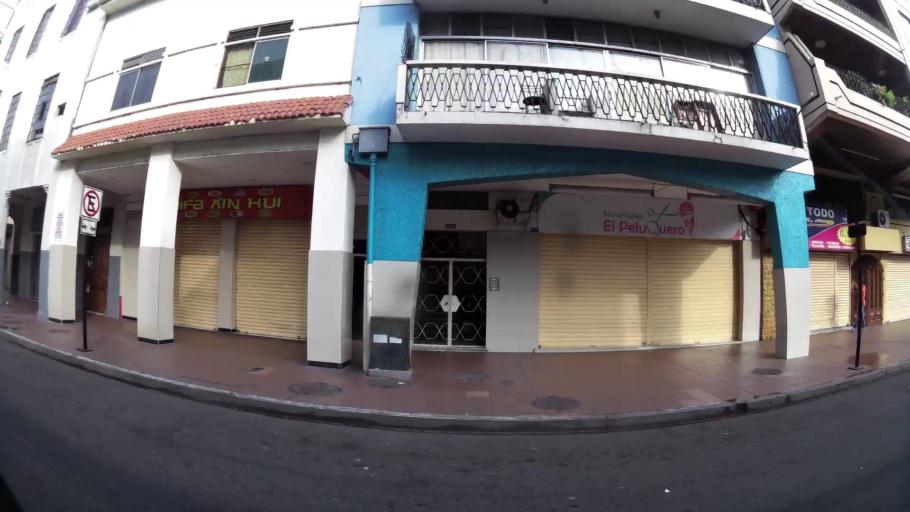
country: EC
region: Guayas
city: Guayaquil
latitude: -2.1924
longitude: -79.8872
